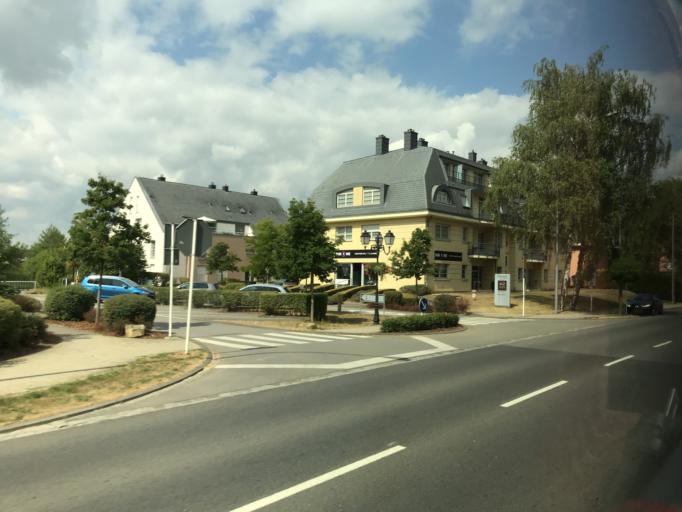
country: LU
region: Luxembourg
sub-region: Canton de Luxembourg
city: Alzingen
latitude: 49.5649
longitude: 6.1622
